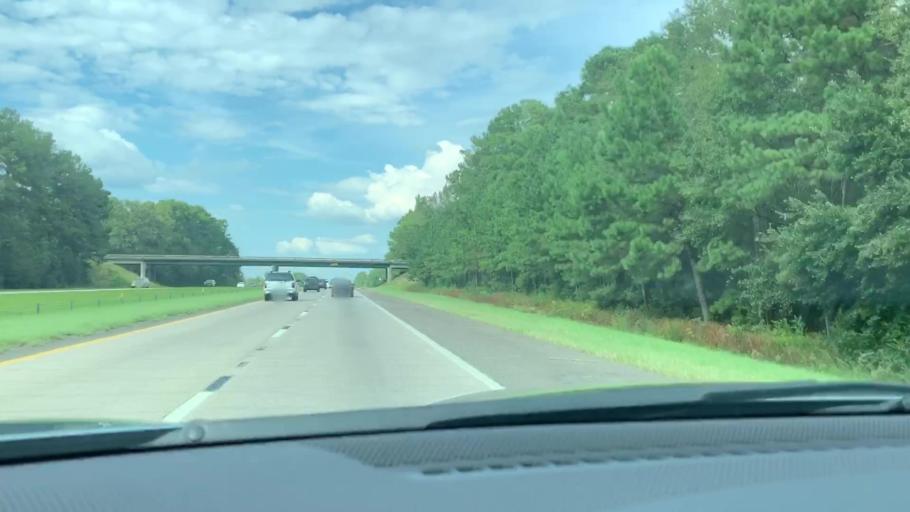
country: US
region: South Carolina
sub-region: Hampton County
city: Yemassee
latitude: 32.6772
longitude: -80.8823
